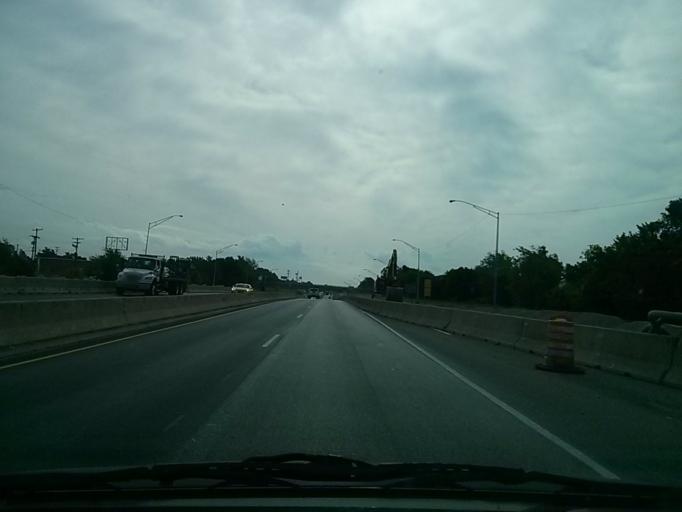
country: US
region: Oklahoma
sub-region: Tulsa County
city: Tulsa
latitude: 36.1594
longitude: -95.9350
